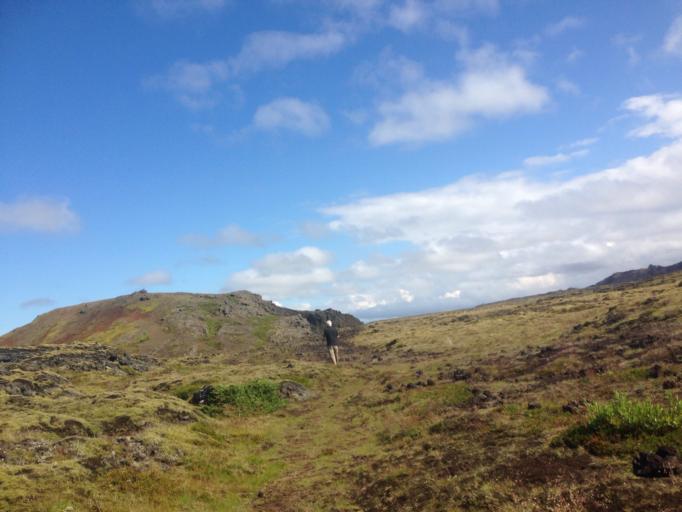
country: IS
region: Capital Region
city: Alftanes
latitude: 63.9515
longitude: -22.0850
